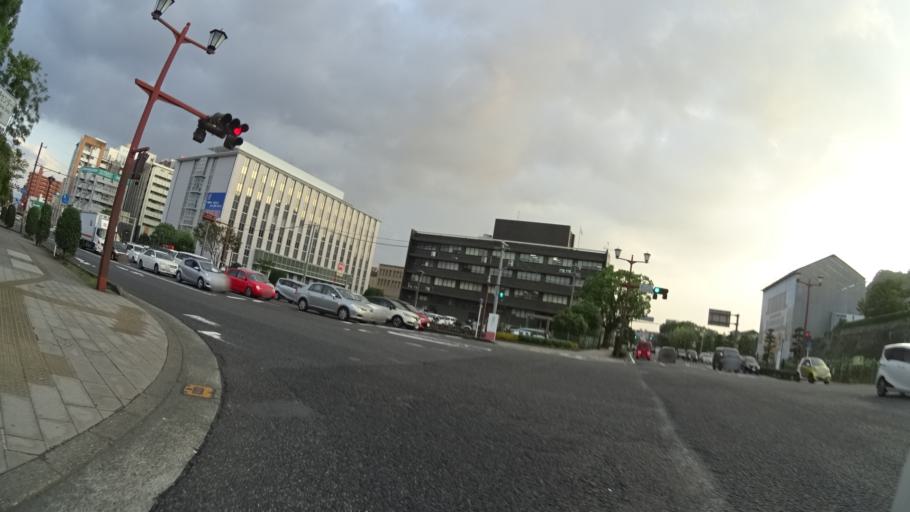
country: JP
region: Kagoshima
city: Kagoshima-shi
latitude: 31.5989
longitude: 130.5566
